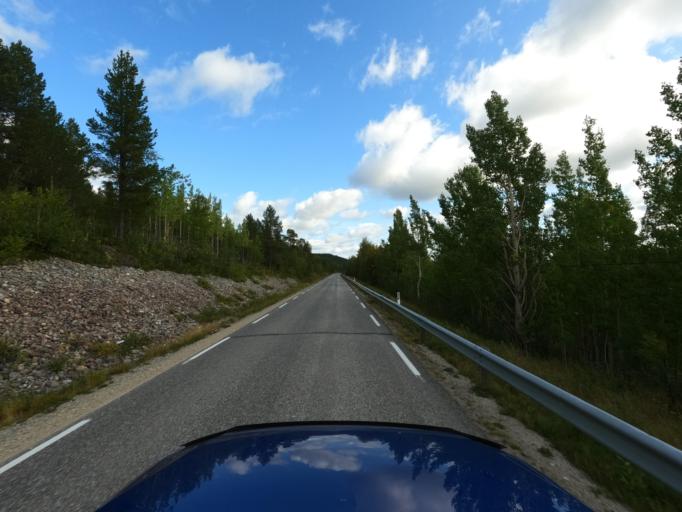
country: NO
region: Finnmark Fylke
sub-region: Karasjok
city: Karasjohka
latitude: 69.4524
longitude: 25.3745
